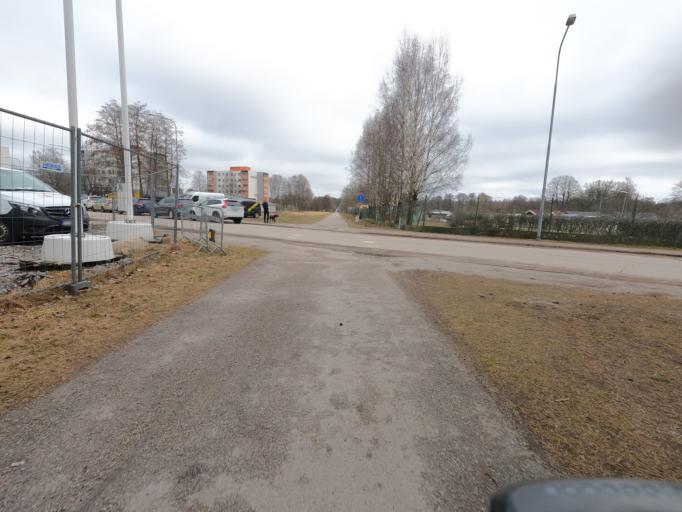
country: SE
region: Kronoberg
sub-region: Ljungby Kommun
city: Ljungby
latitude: 56.8352
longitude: 13.9591
